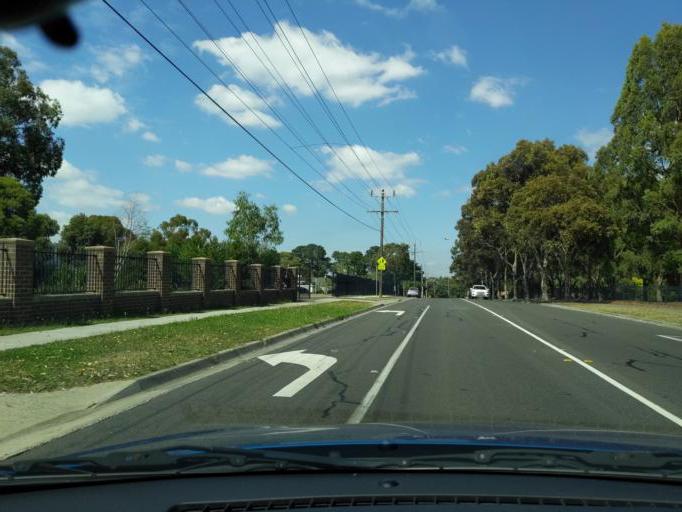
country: AU
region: Victoria
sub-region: Knox
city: Rowville
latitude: -37.9243
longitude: 145.2446
